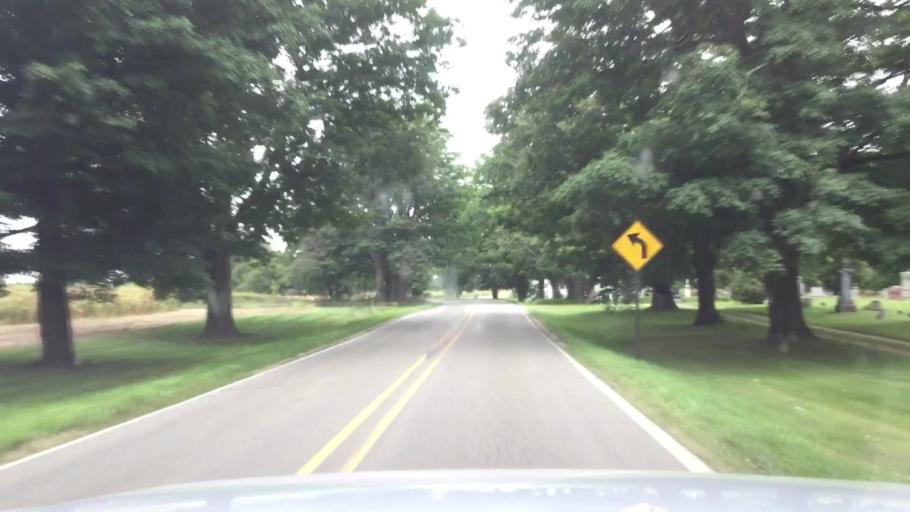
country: US
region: Michigan
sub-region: Shiawassee County
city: Durand
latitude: 42.8283
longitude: -84.0127
